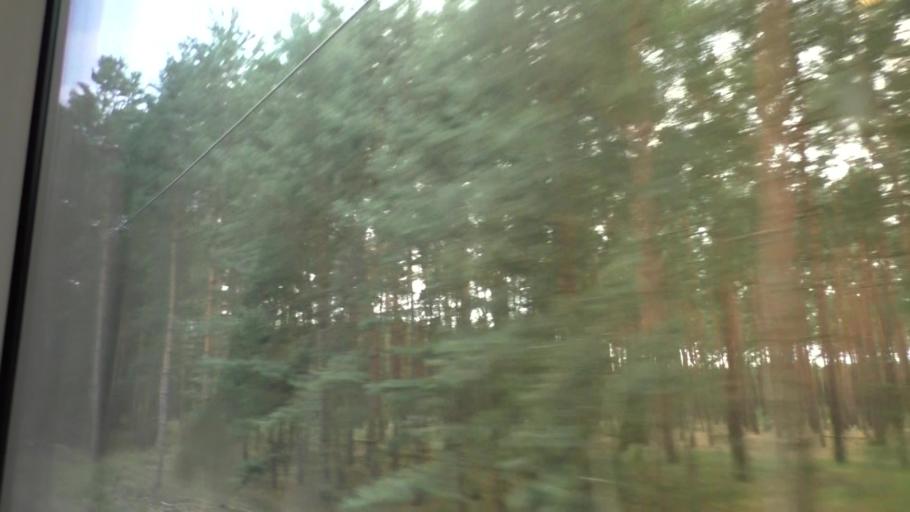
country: DE
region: Brandenburg
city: Storkow
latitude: 52.2618
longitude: 13.9005
